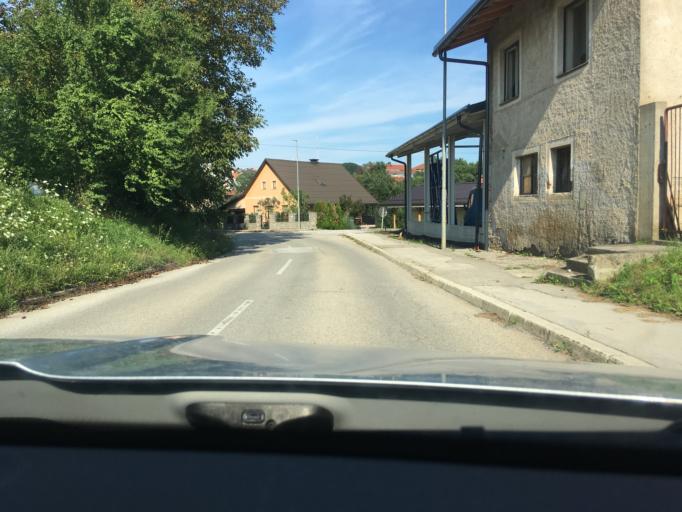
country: SI
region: Crnomelj
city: Crnomelj
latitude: 45.5732
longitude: 15.1864
